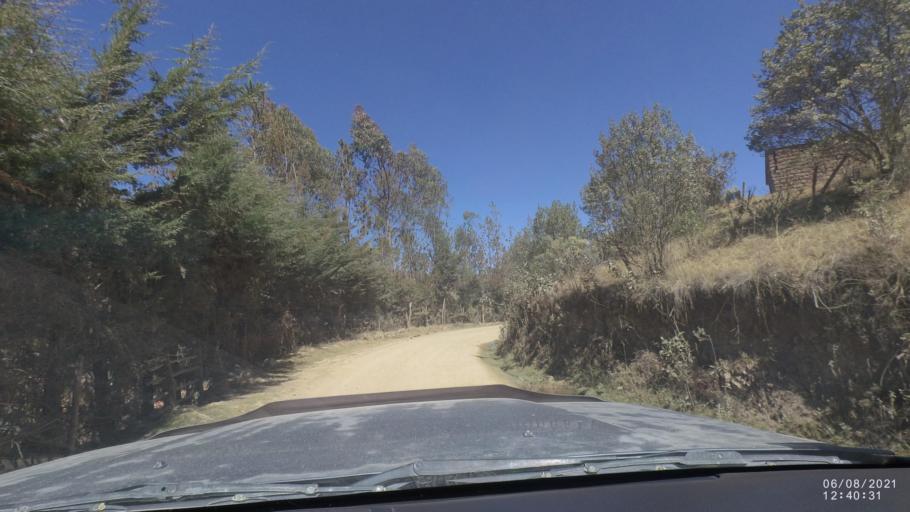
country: BO
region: Cochabamba
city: Colchani
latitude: -16.7841
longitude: -66.6648
